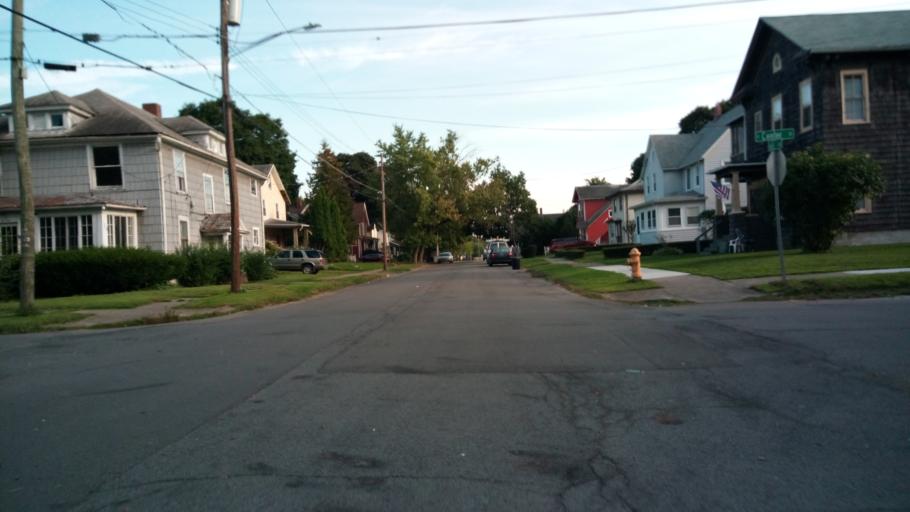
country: US
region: New York
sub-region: Chemung County
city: Elmira
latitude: 42.1091
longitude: -76.8079
